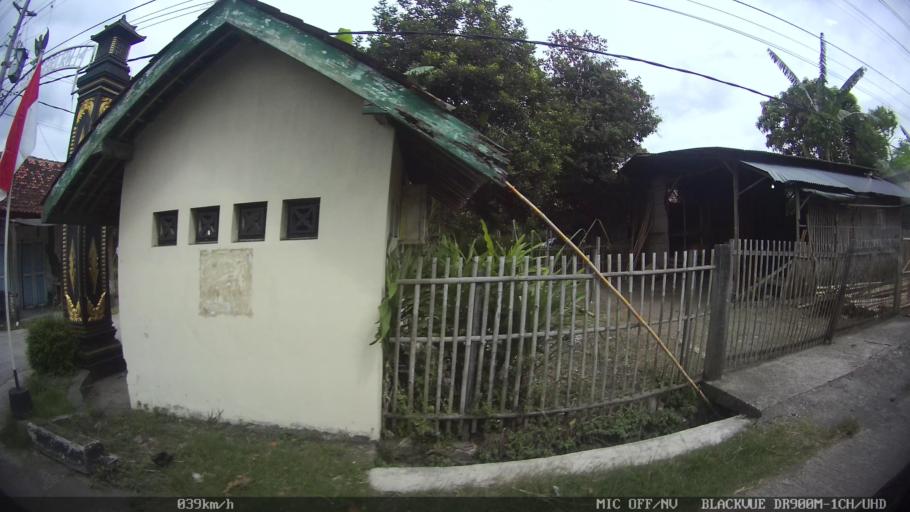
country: ID
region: Daerah Istimewa Yogyakarta
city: Depok
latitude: -7.8154
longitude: 110.4429
